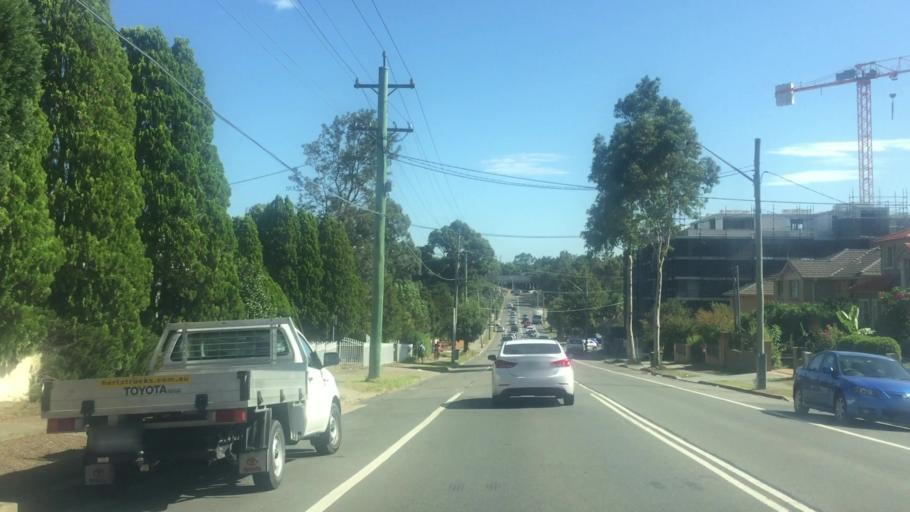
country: AU
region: New South Wales
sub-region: Parramatta
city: City of Parramatta
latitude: -33.8203
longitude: 150.9908
